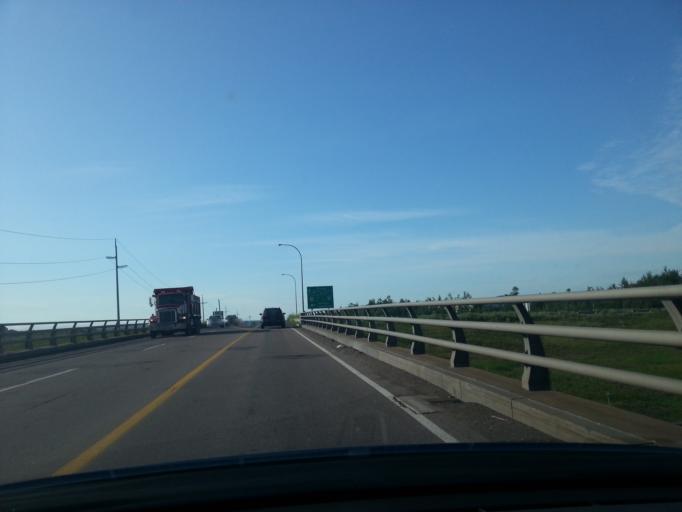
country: CA
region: New Brunswick
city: Dieppe
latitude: 46.1106
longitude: -64.7107
